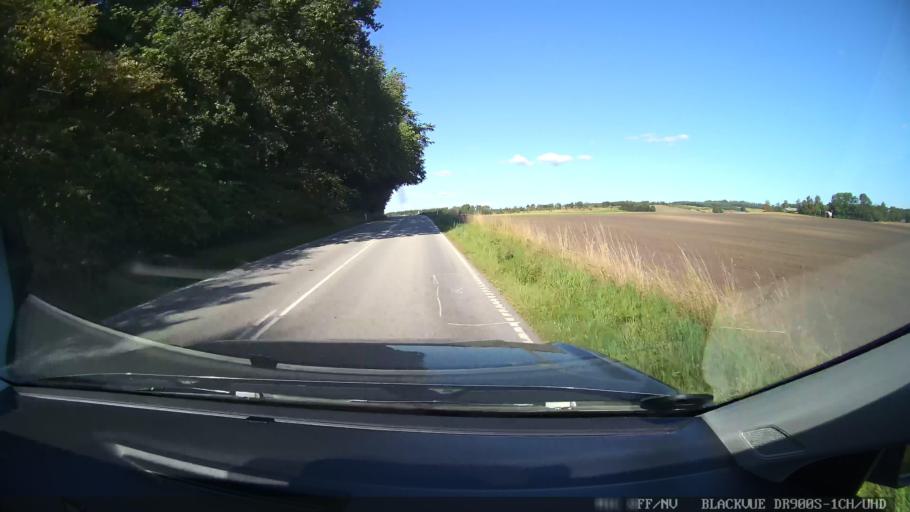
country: DK
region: North Denmark
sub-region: Mariagerfjord Kommune
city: Mariager
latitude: 56.6338
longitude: 9.9787
